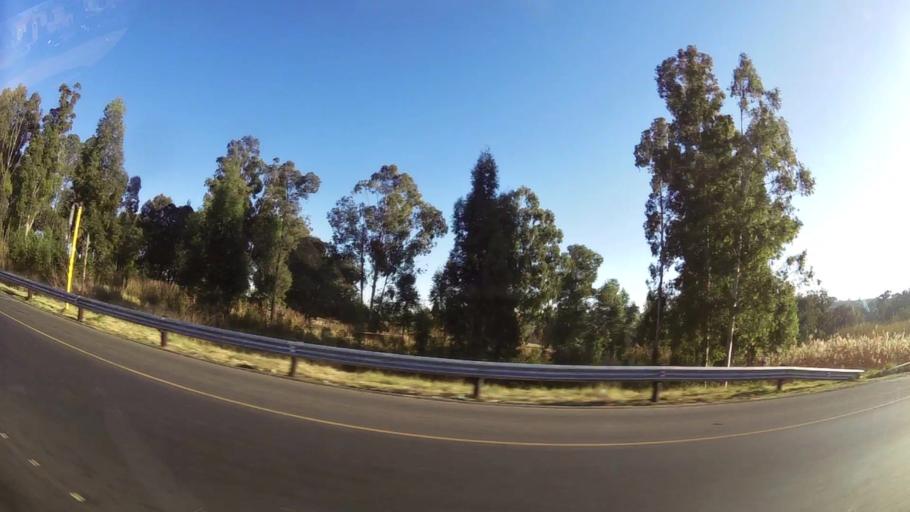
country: ZA
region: Gauteng
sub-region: City of Johannesburg Metropolitan Municipality
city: Modderfontein
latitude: -26.1068
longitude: 28.1677
